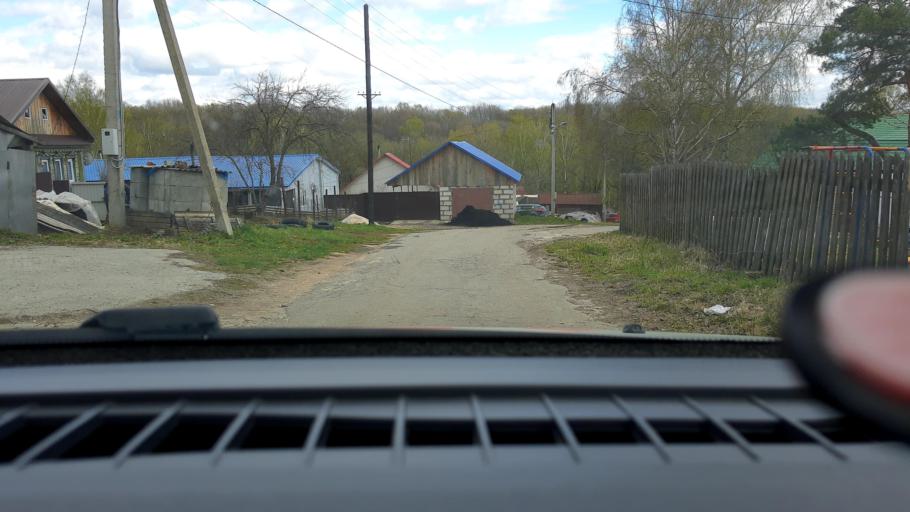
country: RU
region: Nizjnij Novgorod
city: Nizhniy Novgorod
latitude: 56.2065
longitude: 43.9537
